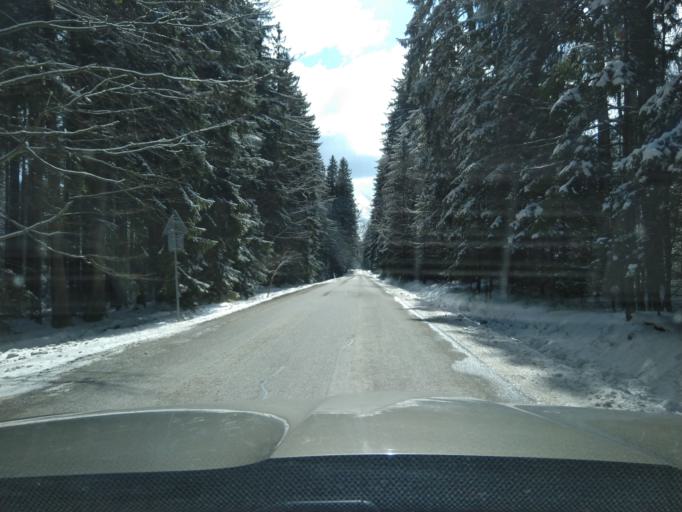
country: CZ
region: Jihocesky
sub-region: Okres Prachatice
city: Stachy
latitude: 49.0556
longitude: 13.6577
